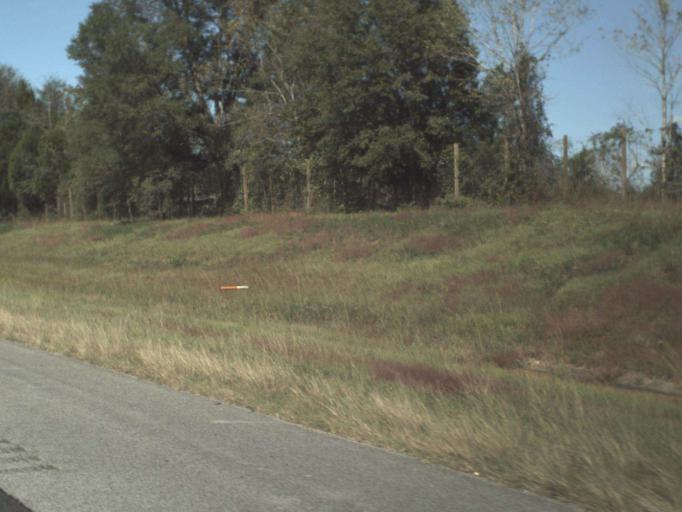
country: US
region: Florida
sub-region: Washington County
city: Chipley
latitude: 30.7518
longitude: -85.5795
